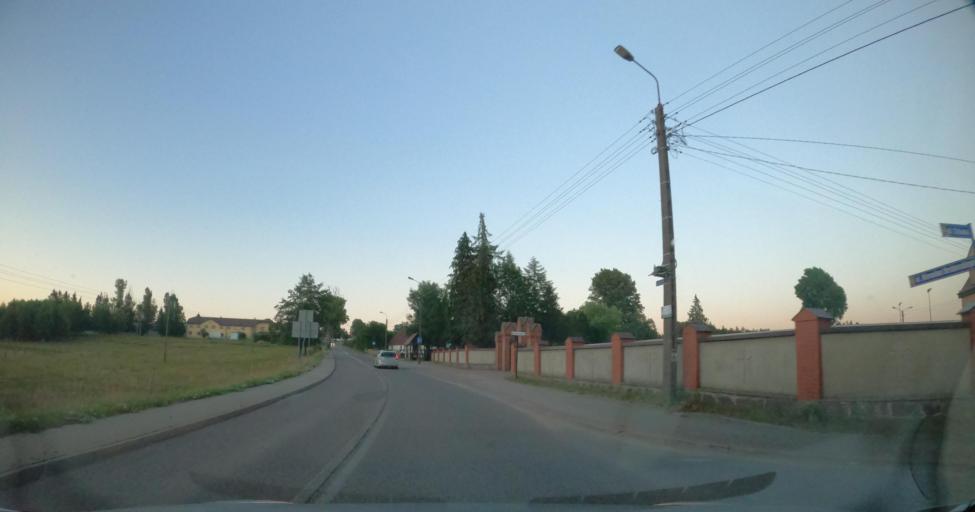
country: PL
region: Pomeranian Voivodeship
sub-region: Powiat wejherowski
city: Linia
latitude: 54.4544
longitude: 18.0300
